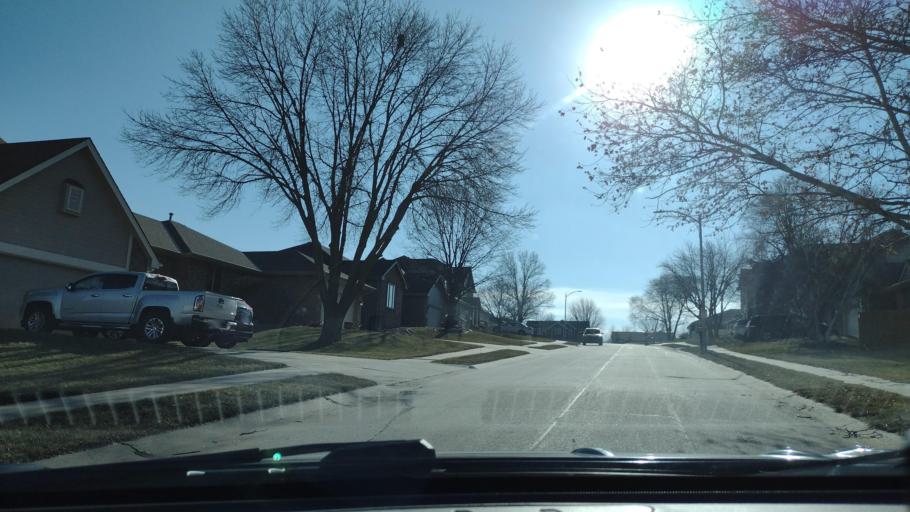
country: US
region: Nebraska
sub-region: Sarpy County
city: Offutt Air Force Base
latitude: 41.1353
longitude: -95.9511
